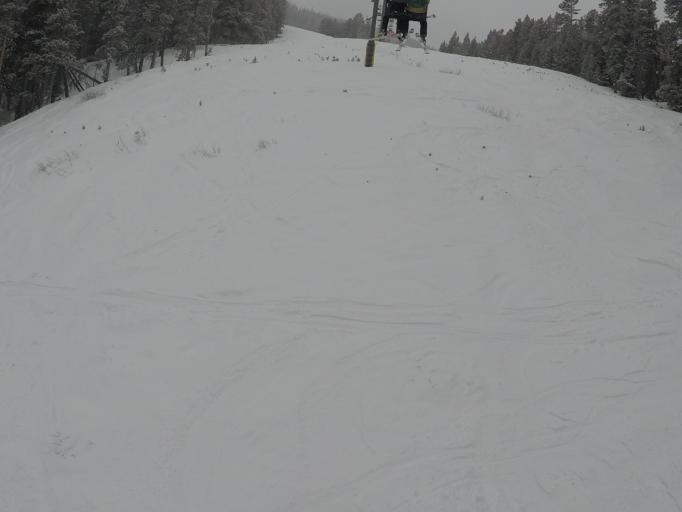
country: US
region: Montana
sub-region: Carbon County
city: Red Lodge
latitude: 45.1880
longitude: -109.3467
